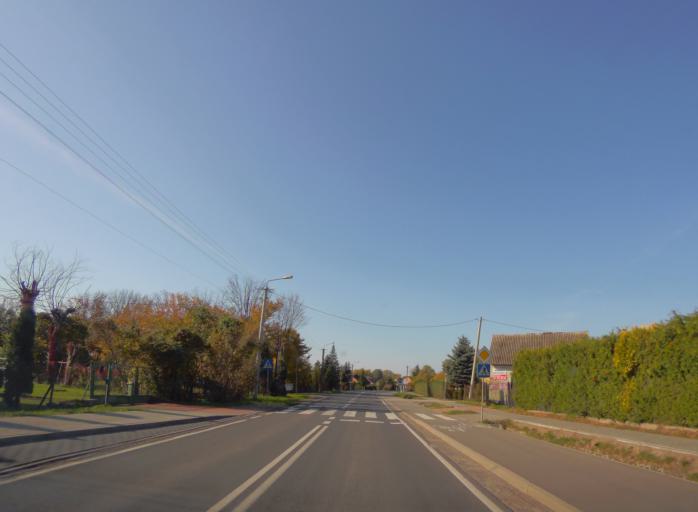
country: PL
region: Masovian Voivodeship
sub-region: Powiat minski
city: Halinow
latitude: 52.1922
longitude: 21.3606
